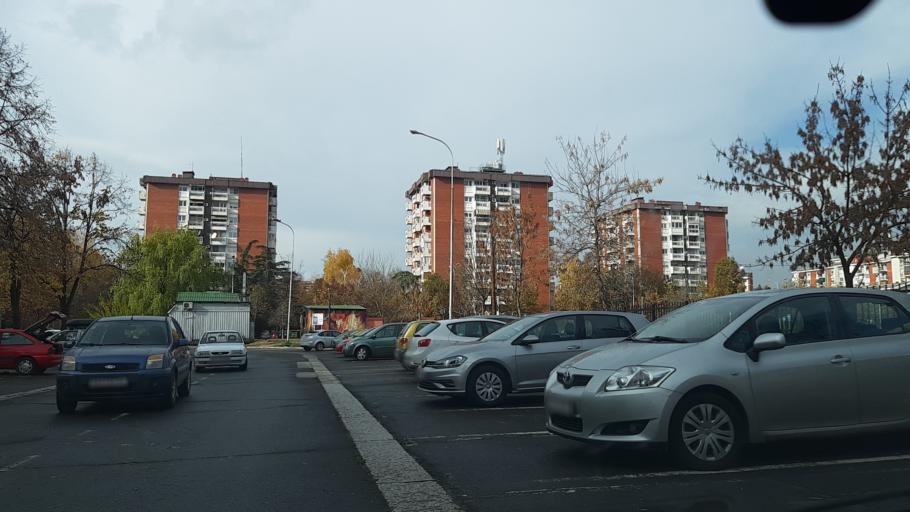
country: MK
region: Kisela Voda
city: Usje
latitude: 41.9890
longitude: 21.4644
